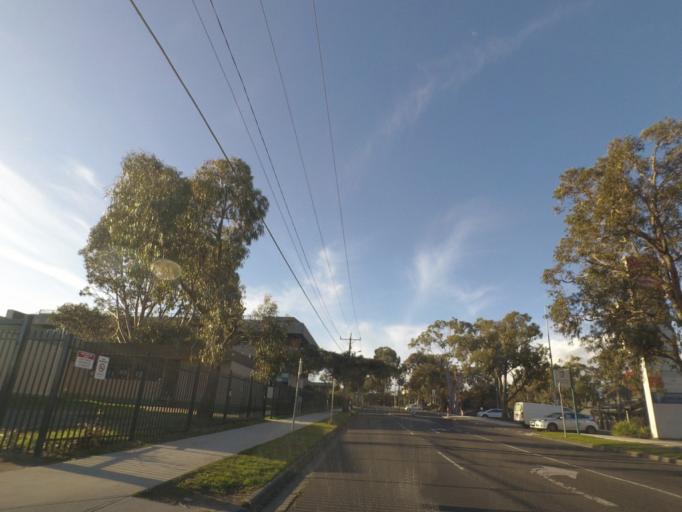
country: AU
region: Victoria
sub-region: Whitehorse
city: Blackburn North
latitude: -37.8118
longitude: 145.1514
